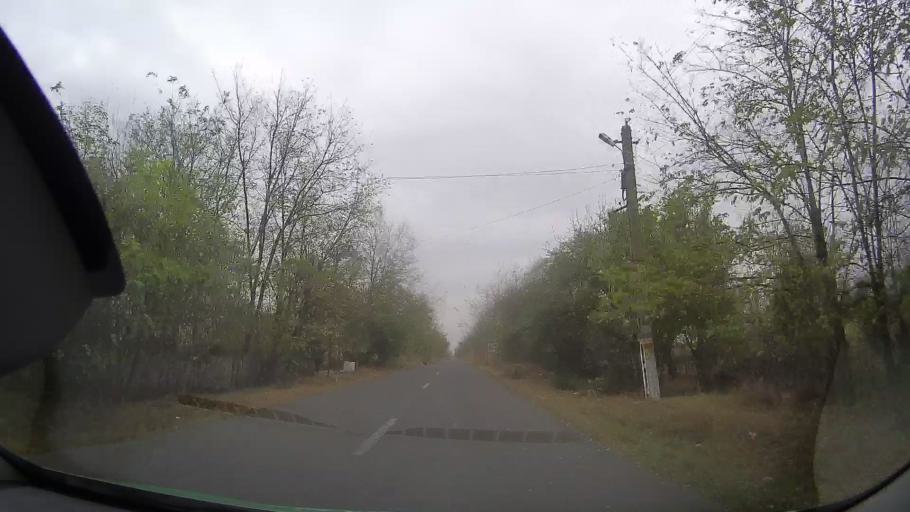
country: RO
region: Buzau
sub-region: Comuna Bradeanu
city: Bradeanu
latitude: 44.9209
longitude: 26.8674
